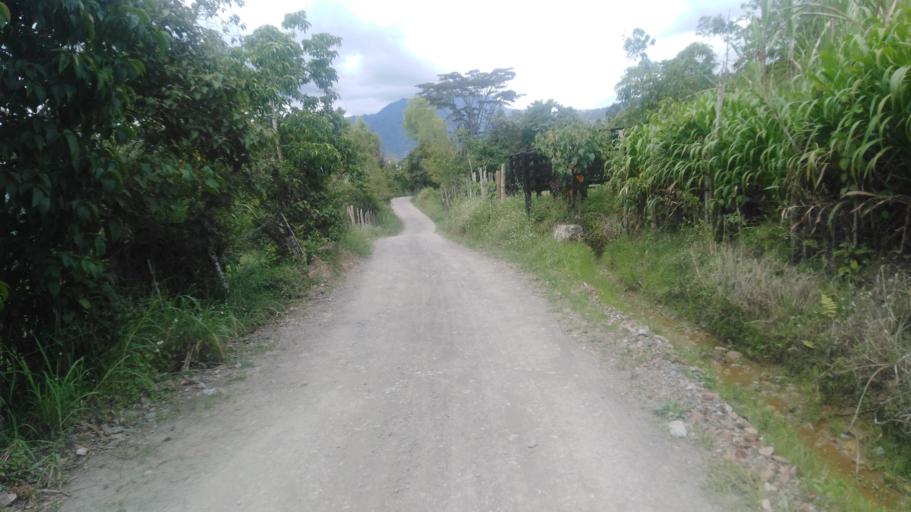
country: CO
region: Cundinamarca
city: Tenza
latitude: 5.0604
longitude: -73.4012
